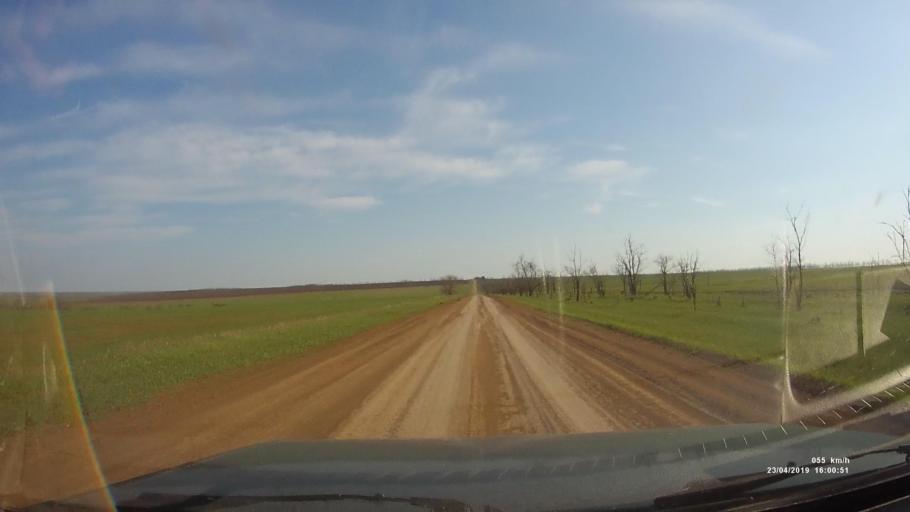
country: RU
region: Rostov
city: Remontnoye
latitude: 46.5043
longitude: 43.1077
